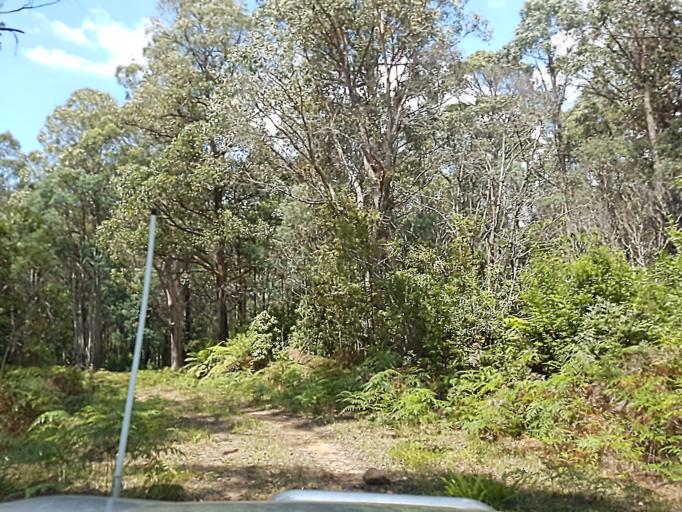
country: AU
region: Victoria
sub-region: East Gippsland
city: Lakes Entrance
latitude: -37.3273
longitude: 148.3255
